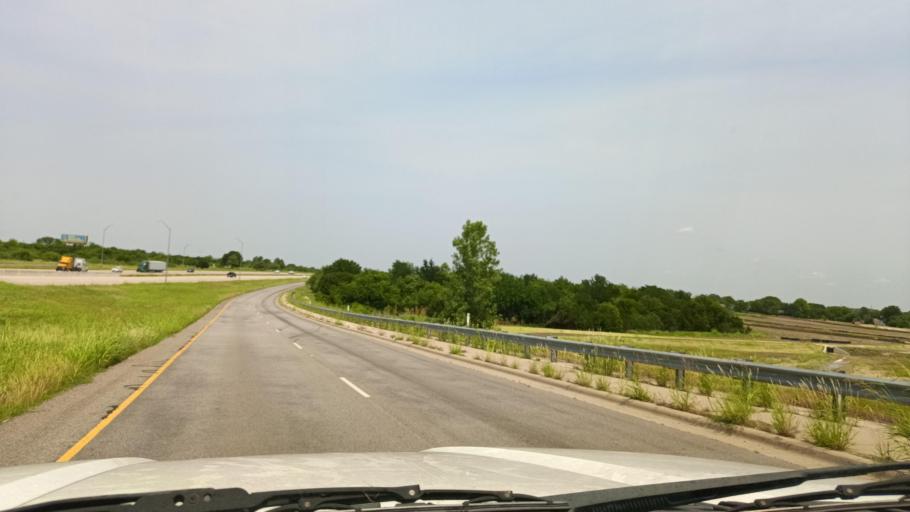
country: US
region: Texas
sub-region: Bell County
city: Temple
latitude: 31.0959
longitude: -97.3905
